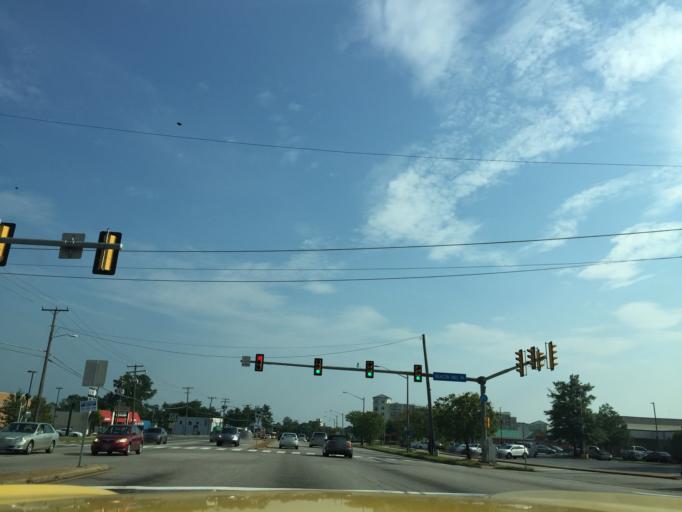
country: US
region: Virginia
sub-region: Fairfax County
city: Groveton
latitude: 38.7726
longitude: -77.0813
